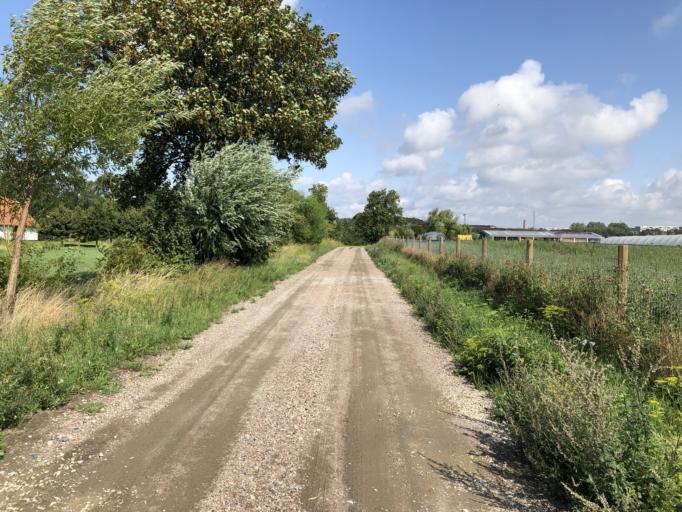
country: SE
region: Skane
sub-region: Malmo
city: Bunkeflostrand
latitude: 55.5515
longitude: 12.9761
